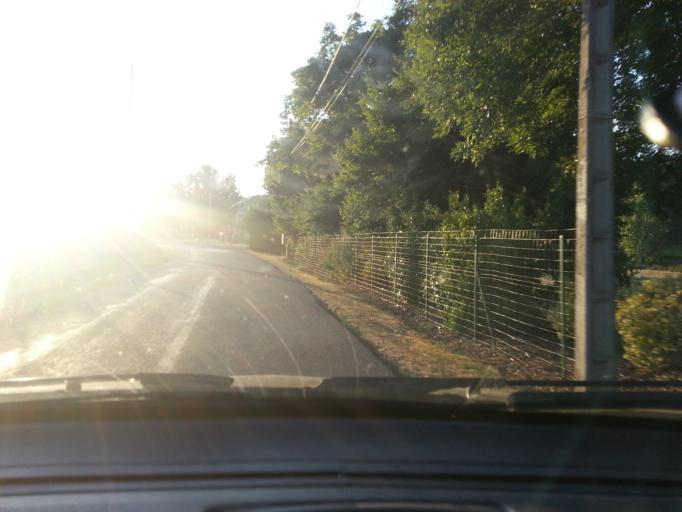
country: FR
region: Bourgogne
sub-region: Departement de Saone-et-Loire
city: Givry
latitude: 46.7666
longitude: 4.7130
